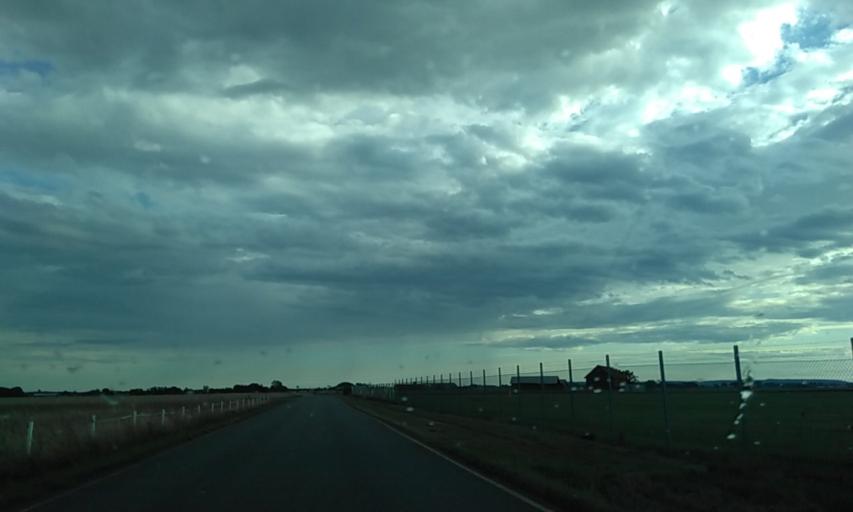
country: SE
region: Vaestra Goetaland
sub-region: Grastorps Kommun
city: Graestorp
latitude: 58.4267
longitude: 12.7302
